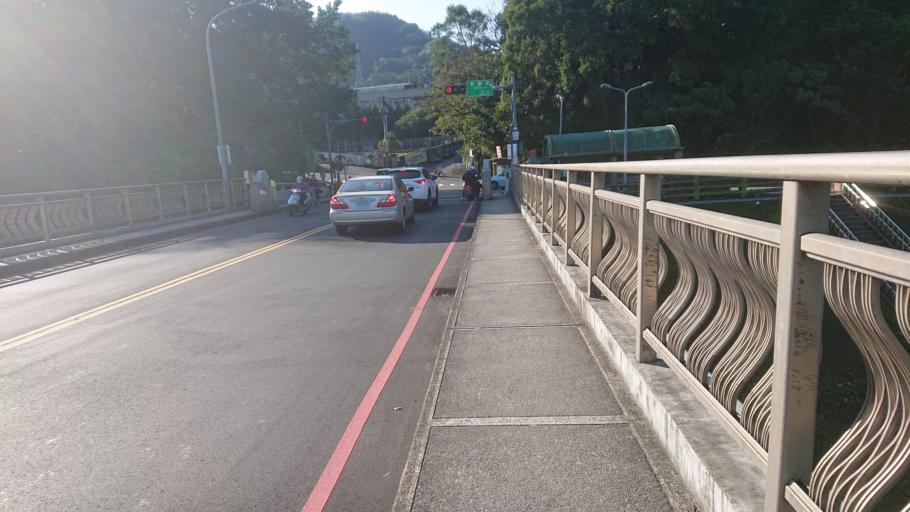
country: TW
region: Taipei
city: Taipei
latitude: 24.9802
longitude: 121.5676
